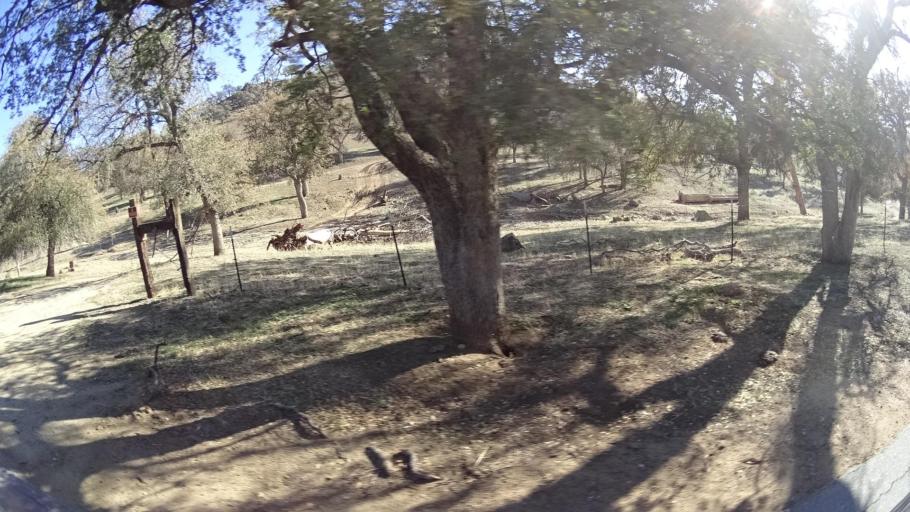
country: US
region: California
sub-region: Kern County
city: Tehachapi
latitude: 35.3316
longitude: -118.3922
